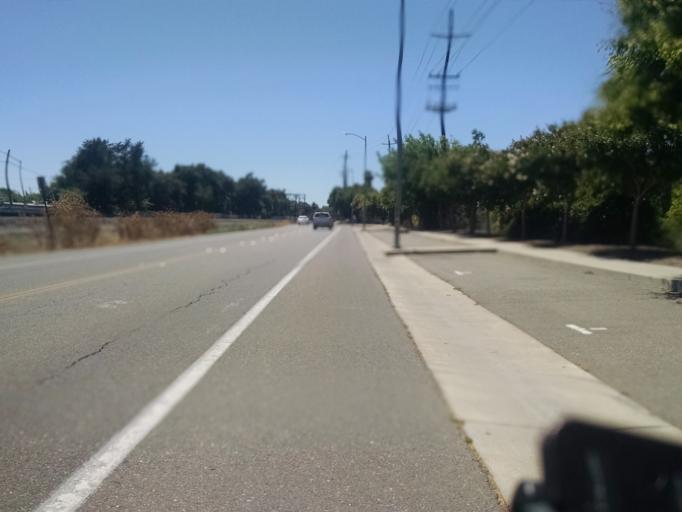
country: US
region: California
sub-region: Yolo County
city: Davis
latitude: 38.5460
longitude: -121.7288
